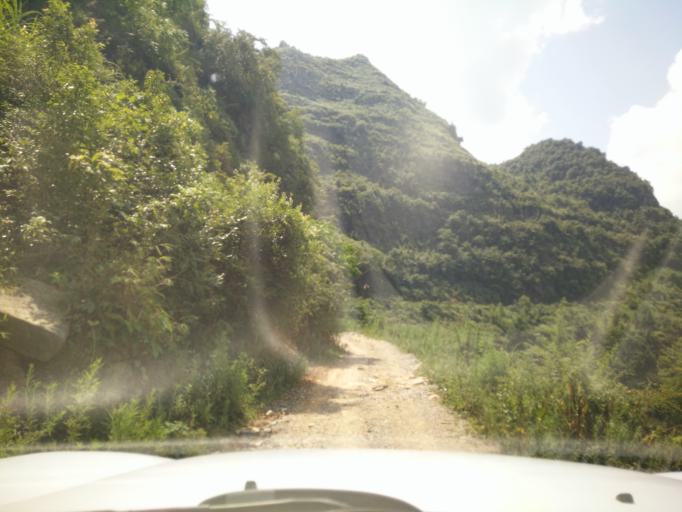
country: CN
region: Guangxi Zhuangzu Zizhiqu
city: Xinzhou
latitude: 25.0206
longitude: 105.7050
